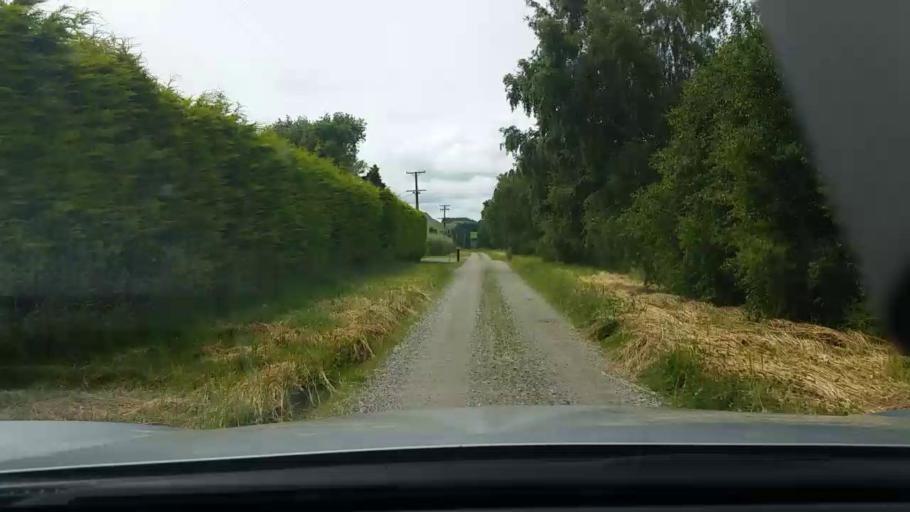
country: NZ
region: Southland
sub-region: Gore District
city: Gore
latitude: -46.1235
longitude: 168.9297
